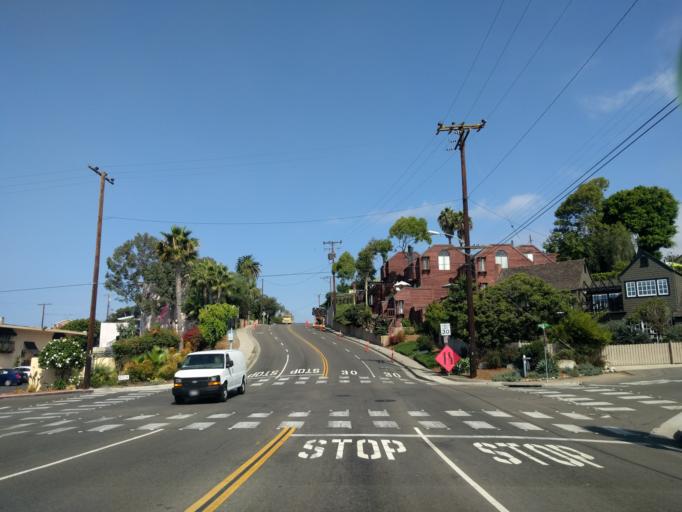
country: US
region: California
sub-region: Orange County
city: Laguna Beach
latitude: 33.5380
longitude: -117.7785
